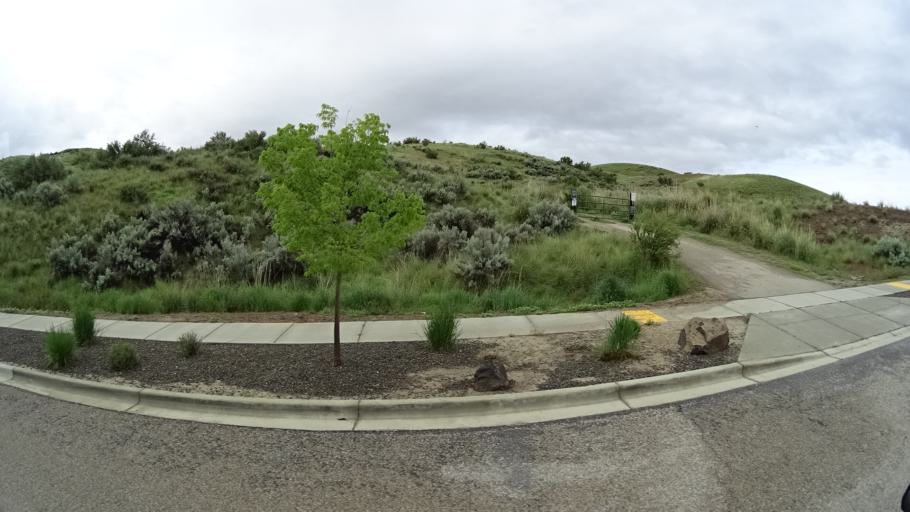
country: US
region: Idaho
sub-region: Ada County
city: Eagle
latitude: 43.7675
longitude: -116.2575
